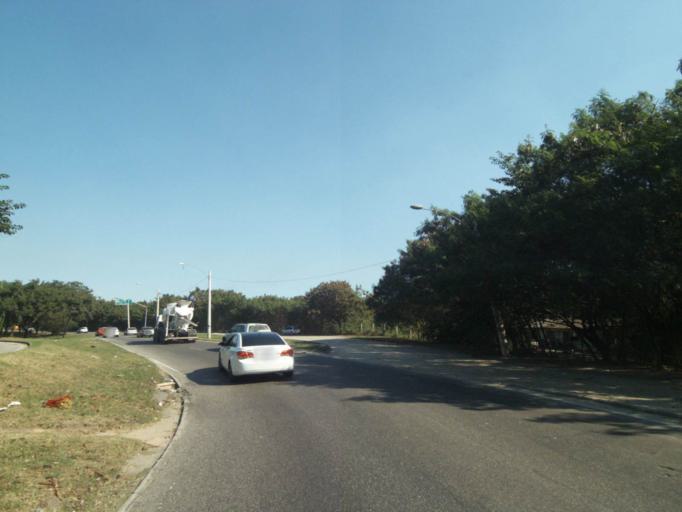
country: BR
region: Rio de Janeiro
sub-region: Sao Joao De Meriti
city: Sao Joao de Meriti
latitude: -22.9547
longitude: -43.3581
